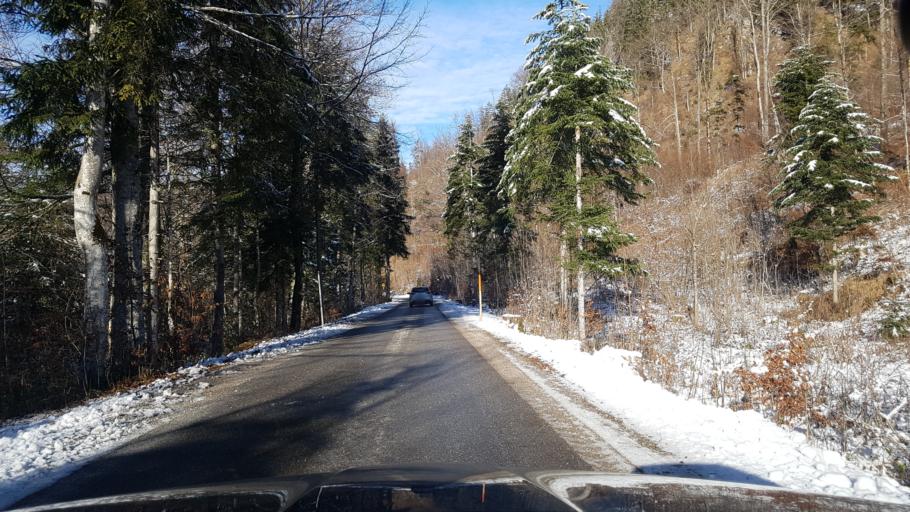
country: AT
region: Salzburg
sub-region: Politischer Bezirk Salzburg-Umgebung
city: Faistenau
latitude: 47.7590
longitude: 13.2308
